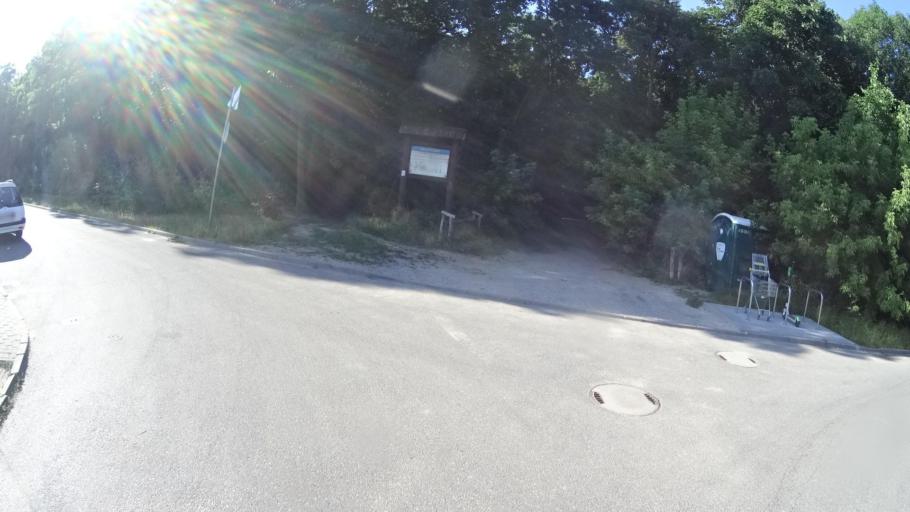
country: PL
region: Masovian Voivodeship
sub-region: Warszawa
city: Bemowo
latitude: 52.2485
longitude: 20.9473
